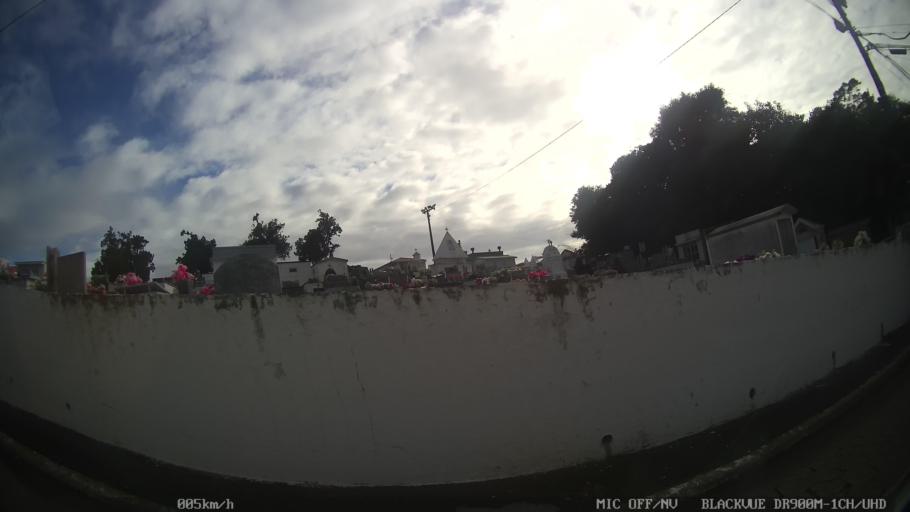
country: BR
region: Santa Catarina
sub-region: Sao Jose
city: Campinas
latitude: -27.6121
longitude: -48.6289
